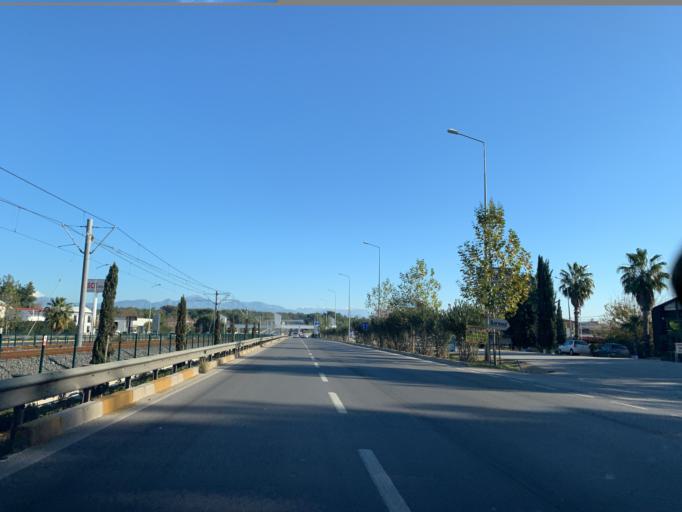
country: TR
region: Antalya
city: Aksu
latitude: 36.9408
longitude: 30.8238
